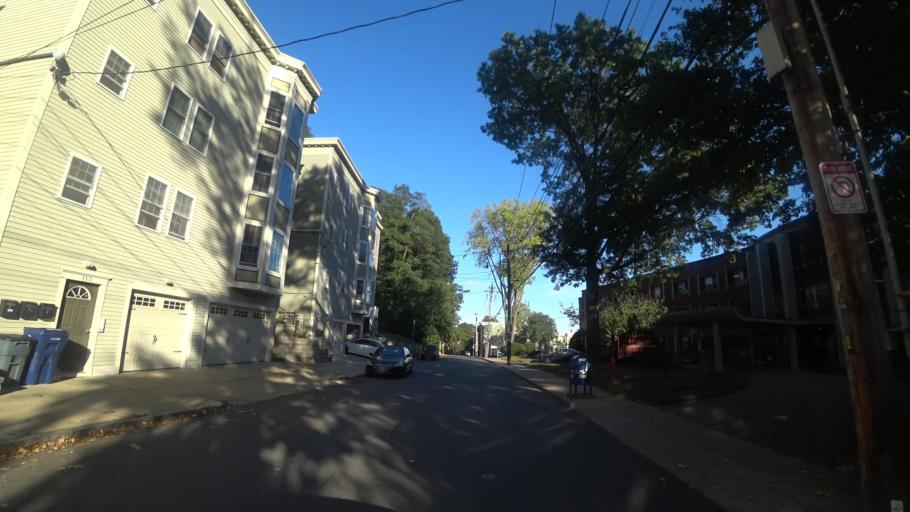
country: US
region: Massachusetts
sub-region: Norfolk County
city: Brookline
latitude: 42.3280
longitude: -71.1054
